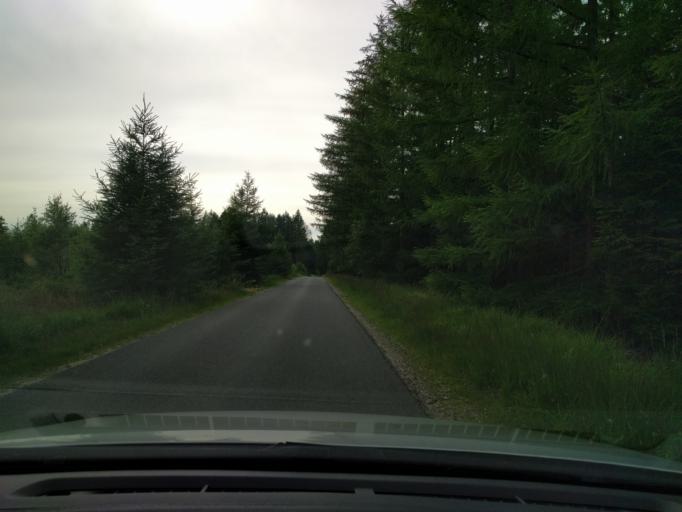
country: DK
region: Central Jutland
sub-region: Herning Kommune
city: Kibaek
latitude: 56.0396
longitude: 8.9170
